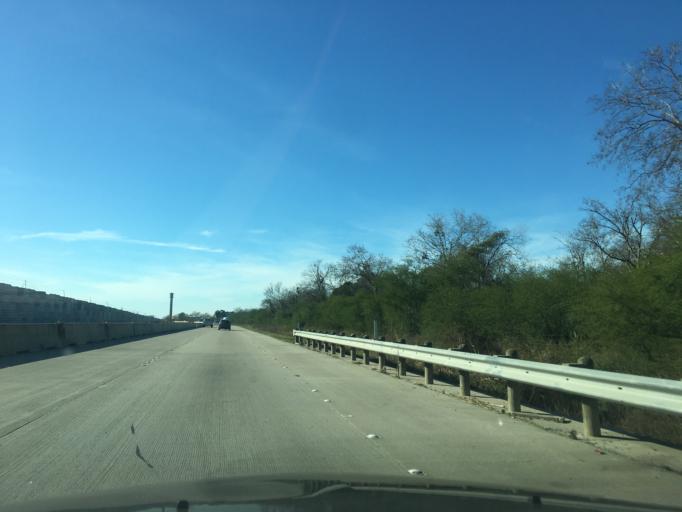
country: US
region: Texas
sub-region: Fort Bend County
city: Rosenberg
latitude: 29.5350
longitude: -95.8464
